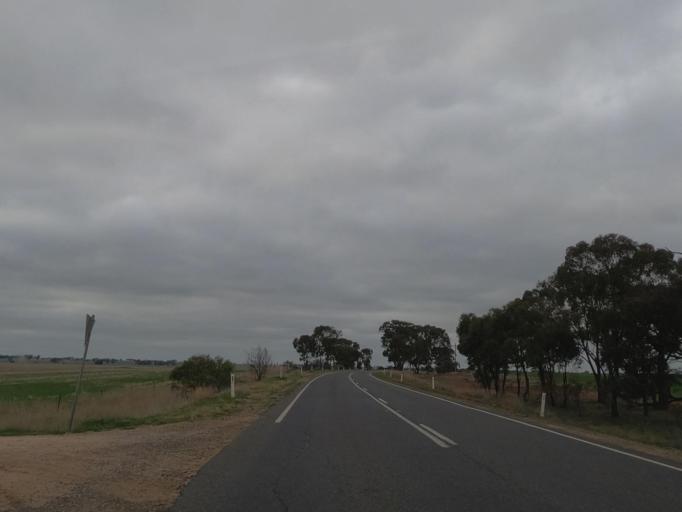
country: AU
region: Victoria
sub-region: Greater Bendigo
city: Long Gully
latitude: -36.5602
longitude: 143.9354
